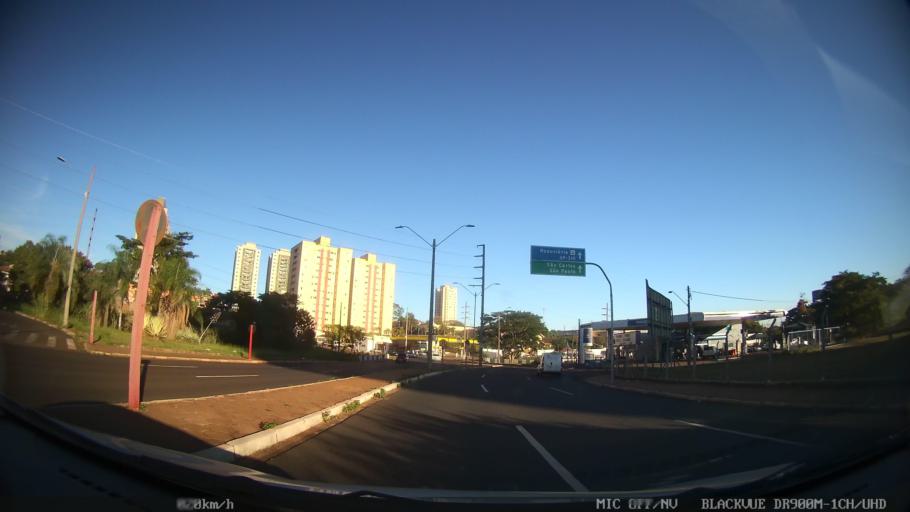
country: BR
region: Sao Paulo
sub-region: Araraquara
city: Araraquara
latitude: -21.8057
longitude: -48.1725
